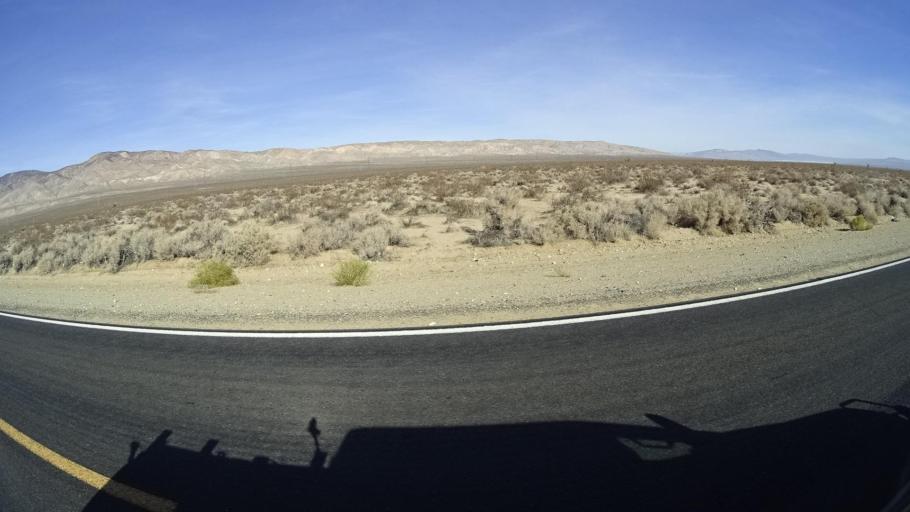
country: US
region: California
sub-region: Kern County
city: Mojave
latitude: 35.1250
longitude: -118.1395
